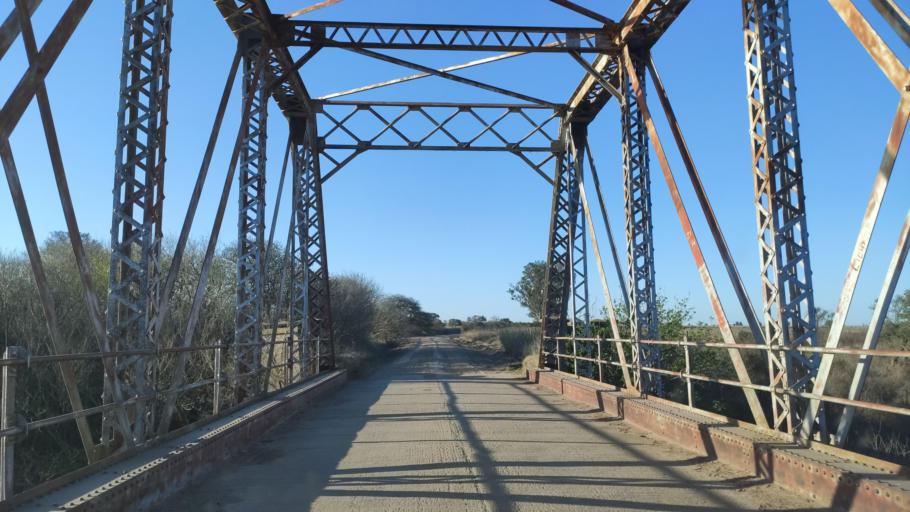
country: AR
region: Cordoba
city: Monte Buey
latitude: -32.8564
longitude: -62.3851
